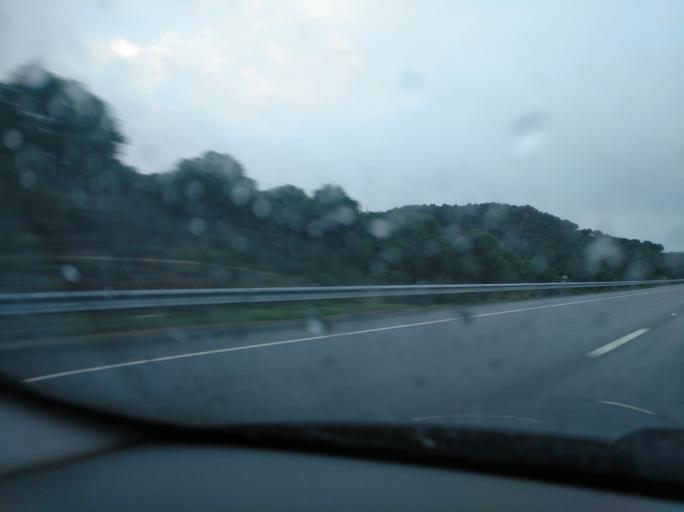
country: PT
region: Faro
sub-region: Alcoutim
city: Alcoutim
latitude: 37.3431
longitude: -7.5055
